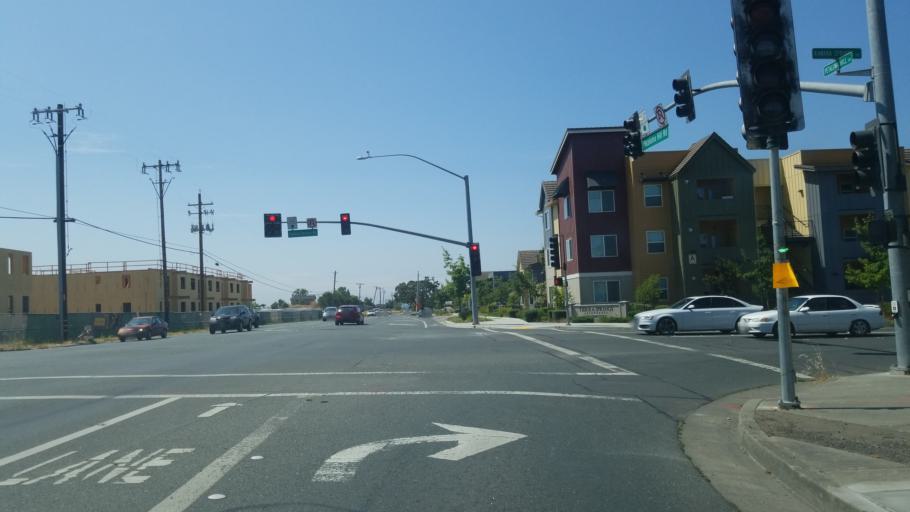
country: US
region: California
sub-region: Sonoma County
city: Roseland
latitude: 38.4167
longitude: -122.7044
